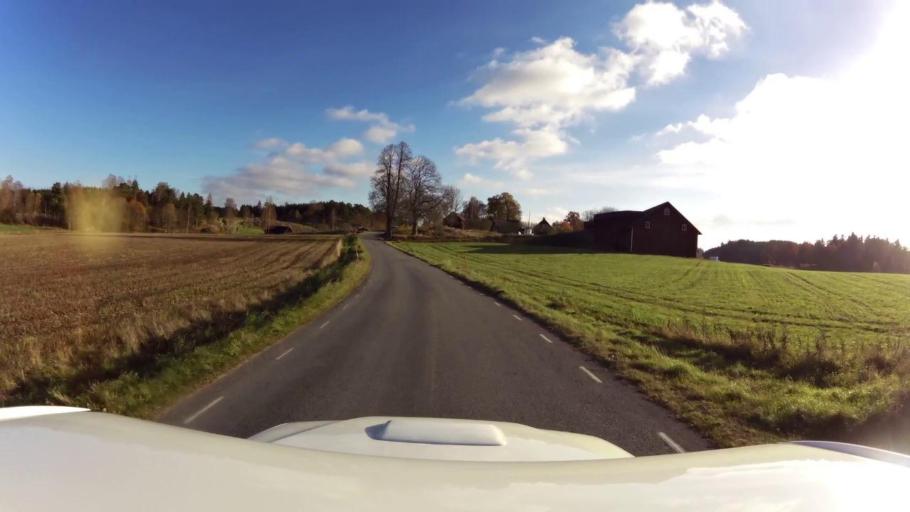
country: SE
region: OEstergoetland
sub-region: Linkopings Kommun
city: Vikingstad
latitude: 58.2571
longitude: 15.4618
